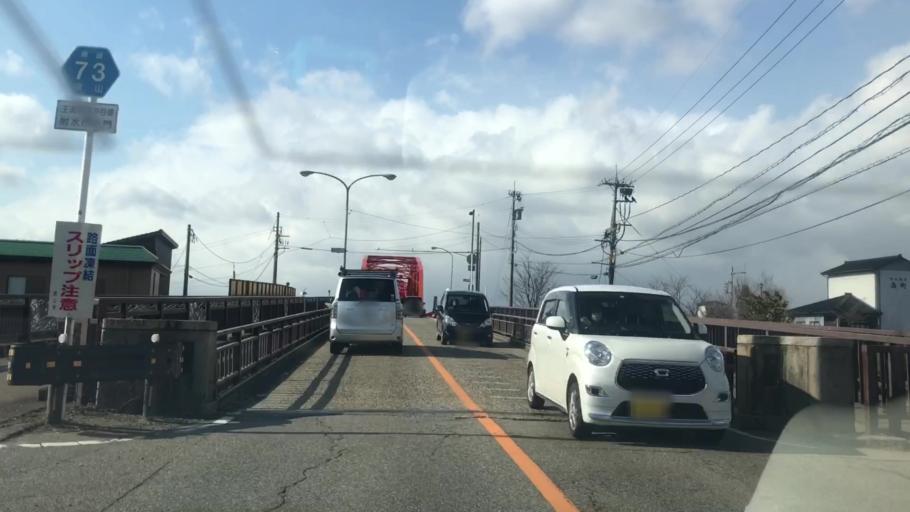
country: JP
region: Toyama
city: Takaoka
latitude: 36.7345
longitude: 137.0461
